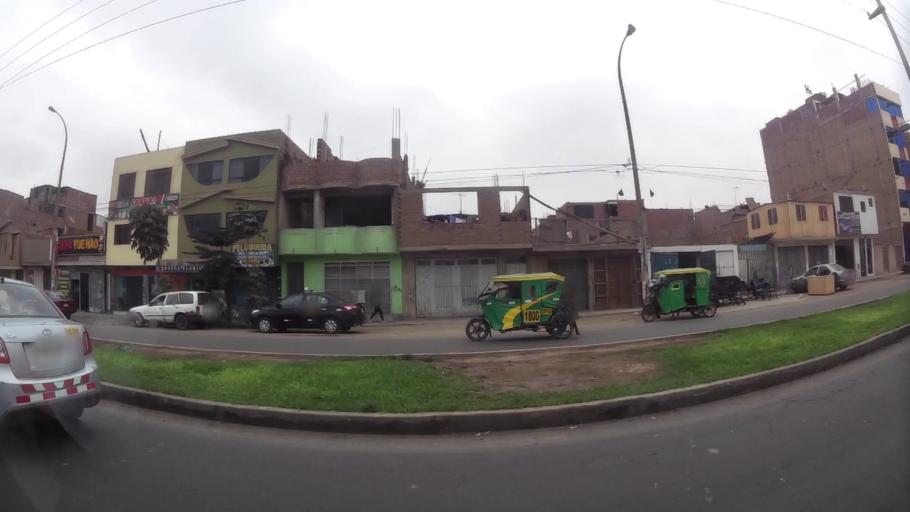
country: PE
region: Lima
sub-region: Lima
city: Independencia
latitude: -11.9492
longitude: -77.0819
